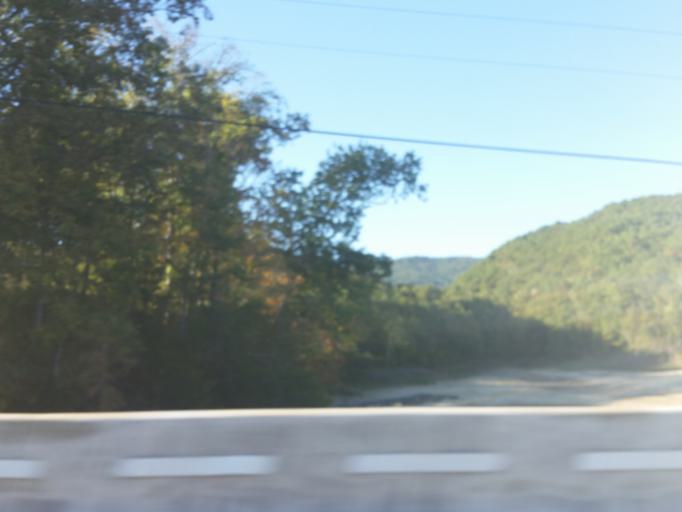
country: US
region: Tennessee
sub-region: Grainger County
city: Bean Station
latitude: 36.3329
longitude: -83.3618
